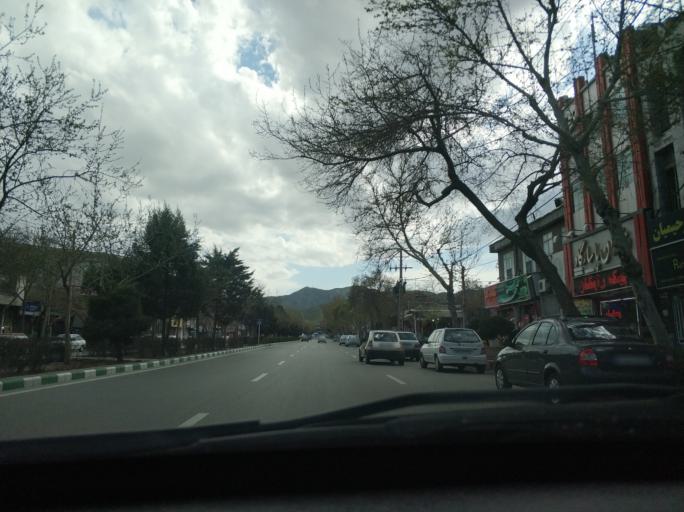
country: IR
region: Razavi Khorasan
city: Mashhad
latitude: 36.2693
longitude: 59.5883
